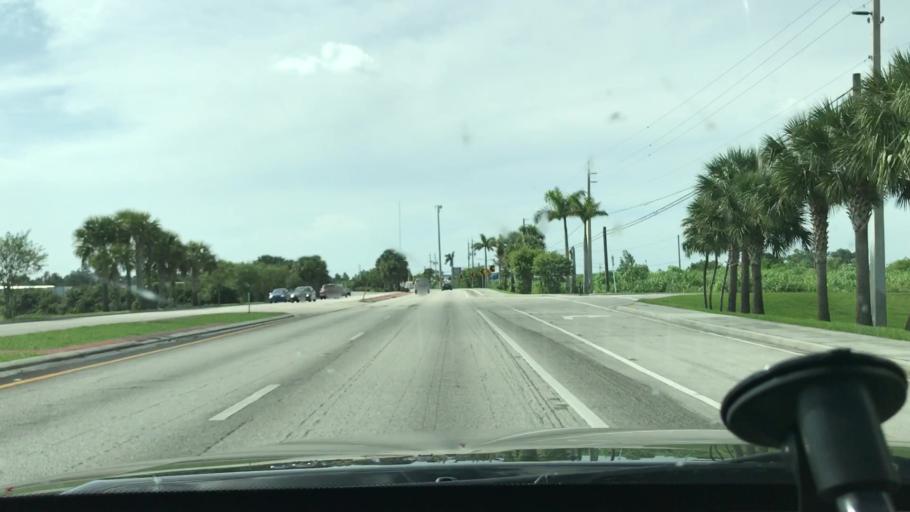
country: US
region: Florida
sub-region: Palm Beach County
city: South Bay
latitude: 26.6733
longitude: -80.7208
